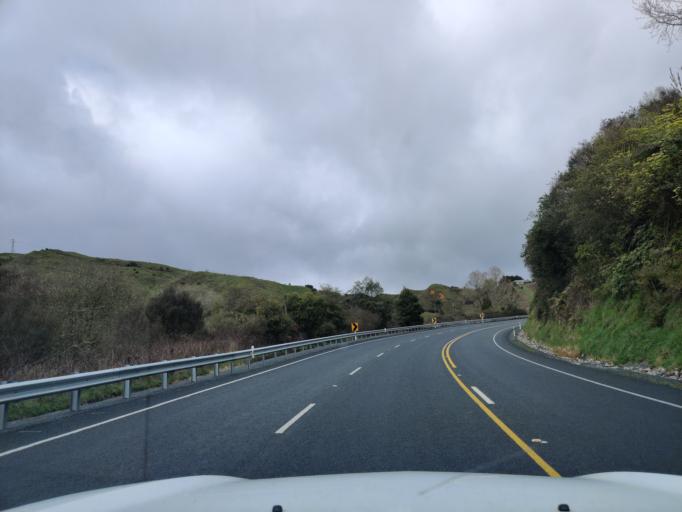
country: NZ
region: Waikato
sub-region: Otorohanga District
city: Otorohanga
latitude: -38.6338
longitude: 175.2089
